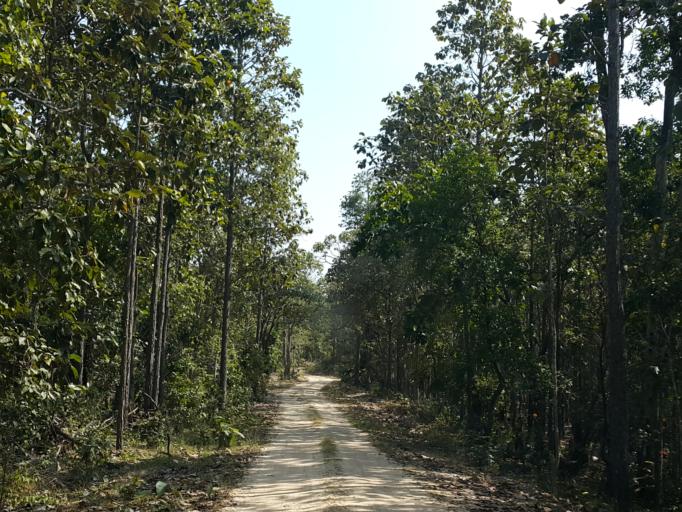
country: TH
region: Chiang Mai
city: Hot
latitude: 18.1333
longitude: 98.4283
